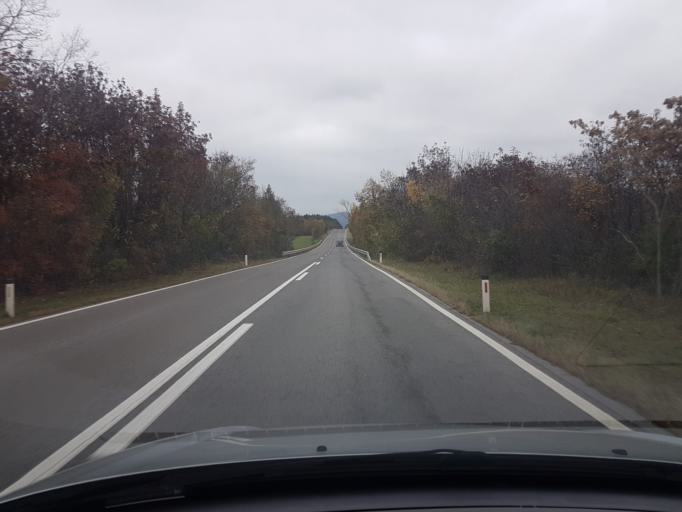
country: SI
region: Sezana
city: Sezana
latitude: 45.7190
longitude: 13.8948
